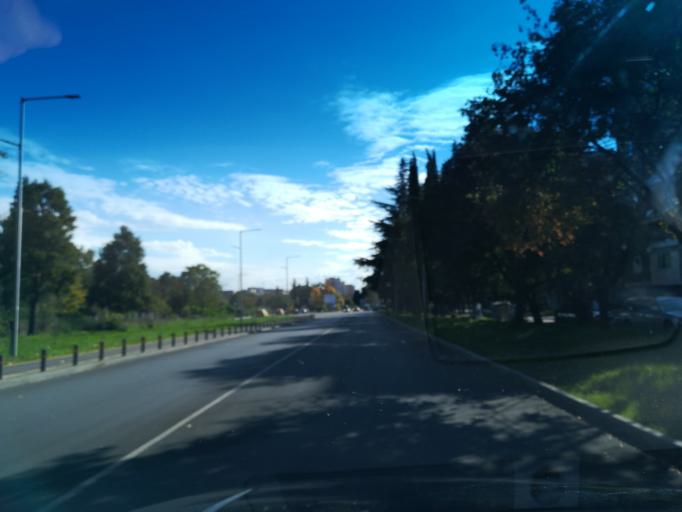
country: BG
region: Stara Zagora
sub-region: Obshtina Stara Zagora
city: Stara Zagora
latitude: 42.4353
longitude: 25.6366
